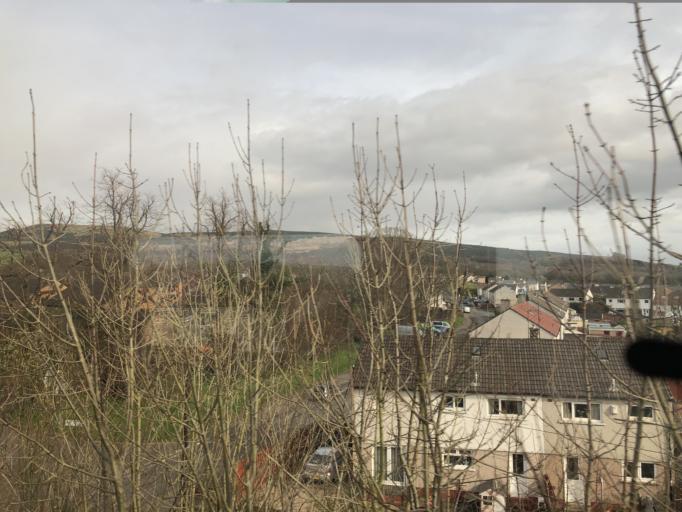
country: GB
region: Scotland
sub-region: Argyll and Bute
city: Helensburgh
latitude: 55.9996
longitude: -4.7125
